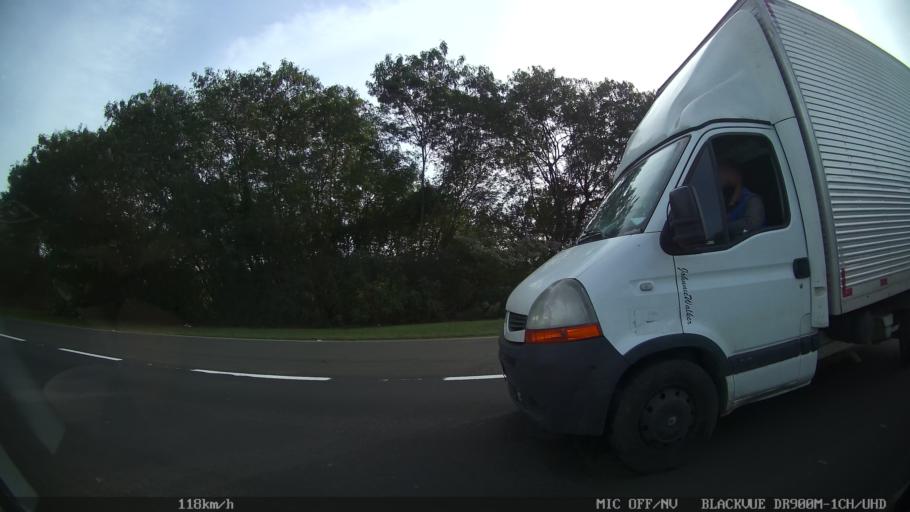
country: BR
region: Sao Paulo
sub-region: Piracicaba
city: Piracicaba
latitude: -22.7232
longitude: -47.5904
